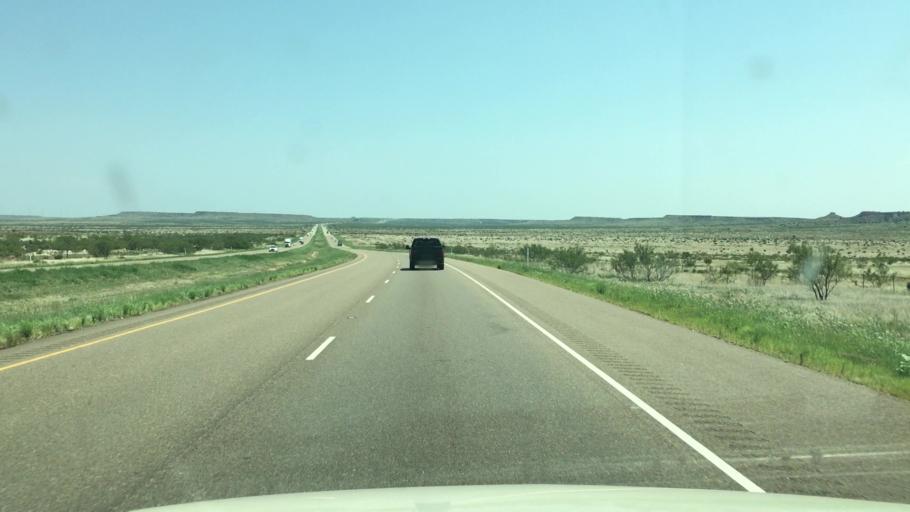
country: US
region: Texas
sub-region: Oldham County
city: Vega
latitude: 35.2258
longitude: -102.8687
